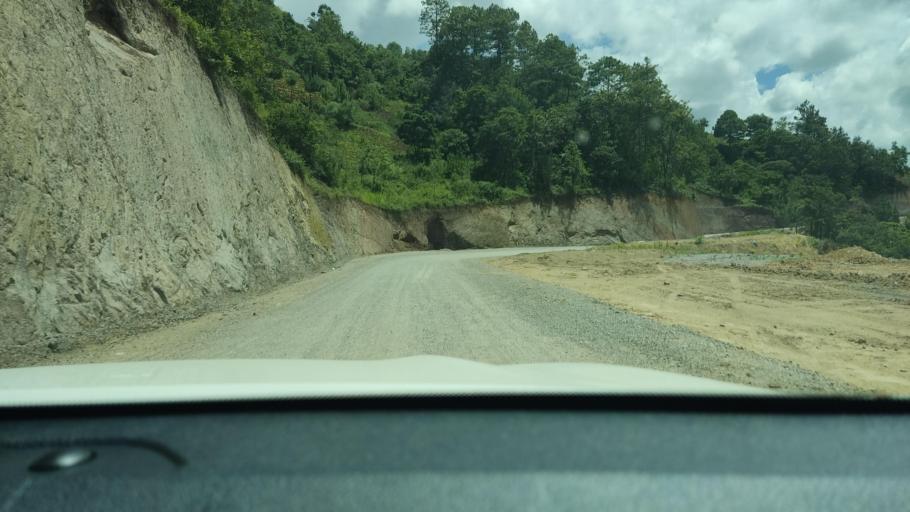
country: GT
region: Chimaltenango
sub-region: Municipio de San Juan Comalapa
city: Comalapa
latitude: 14.7886
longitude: -90.8603
